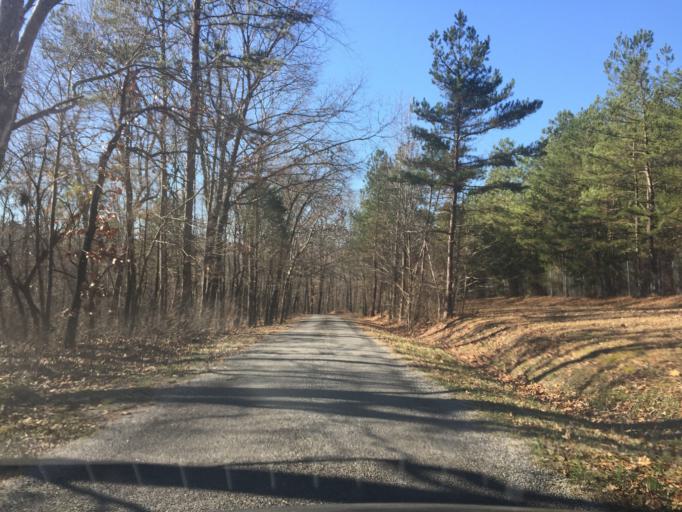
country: US
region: Tennessee
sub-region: Hamilton County
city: Harrison
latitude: 35.0985
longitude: -85.1136
